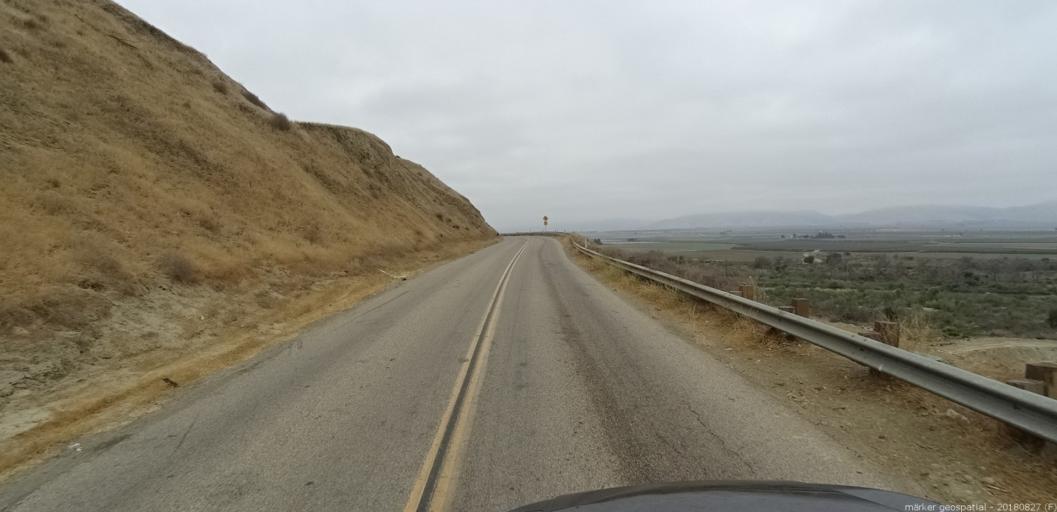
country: US
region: California
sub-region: Monterey County
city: Greenfield
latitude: 36.3220
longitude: -121.1823
